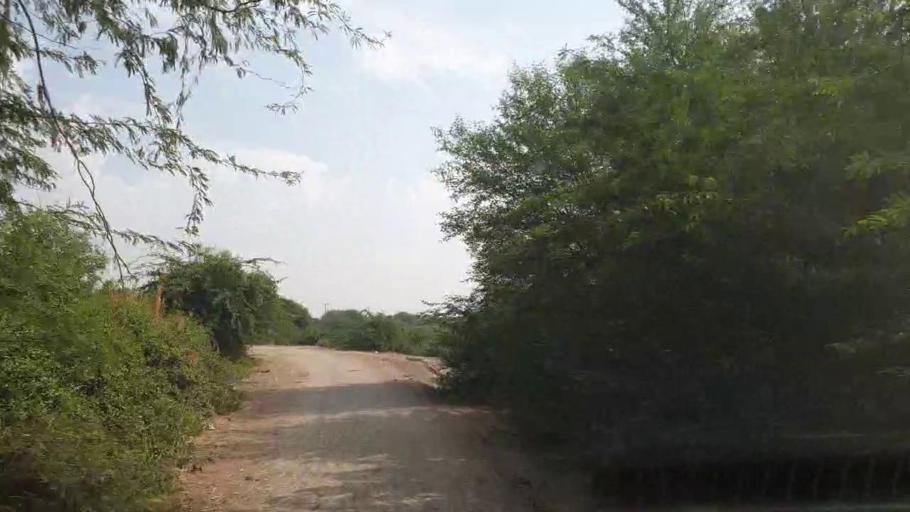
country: PK
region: Sindh
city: Tando Bago
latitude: 24.9329
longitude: 69.0046
